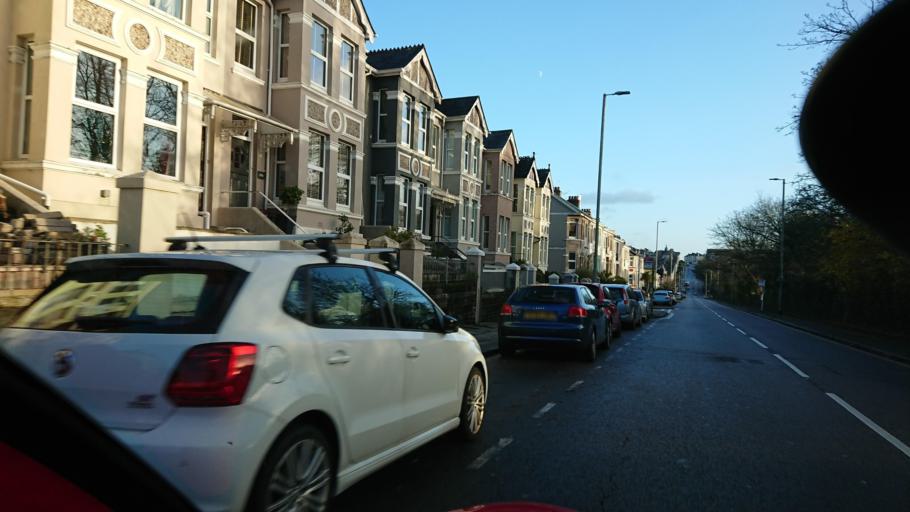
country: GB
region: England
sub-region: Plymouth
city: Plymouth
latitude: 50.3923
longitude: -4.1441
